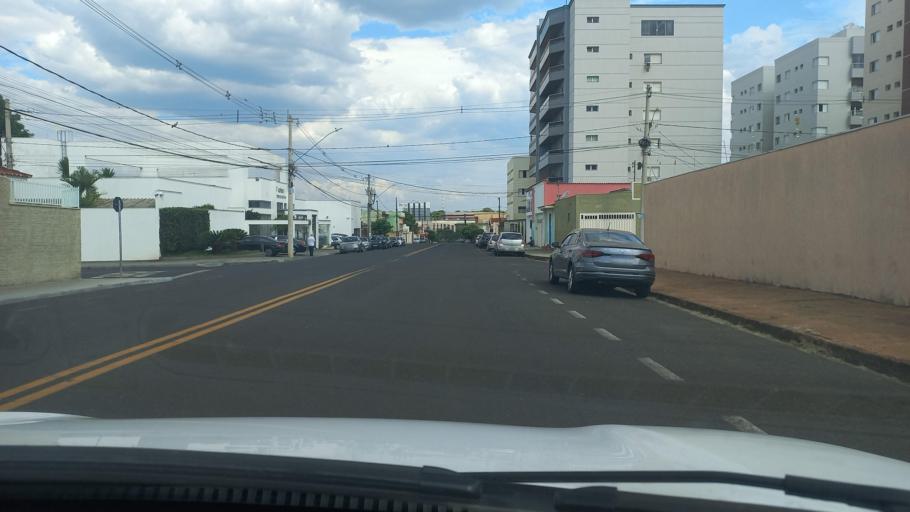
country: BR
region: Minas Gerais
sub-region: Uberaba
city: Uberaba
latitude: -19.7620
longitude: -47.9545
